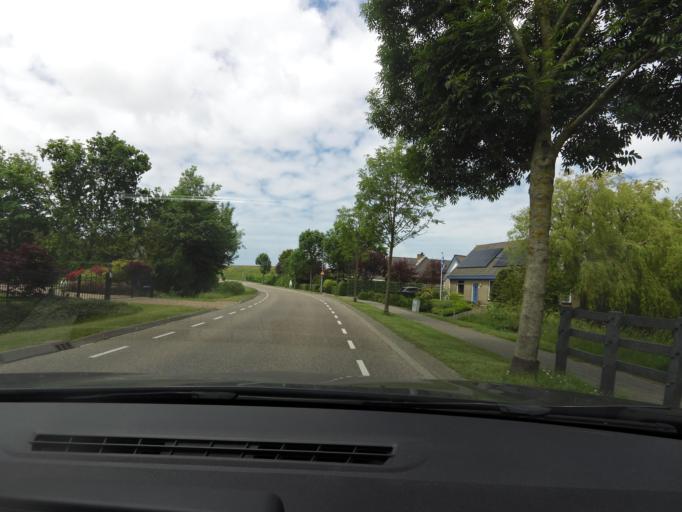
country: NL
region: Zeeland
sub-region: Schouwen-Duiveland
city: Scharendijke
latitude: 51.7374
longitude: 3.8381
